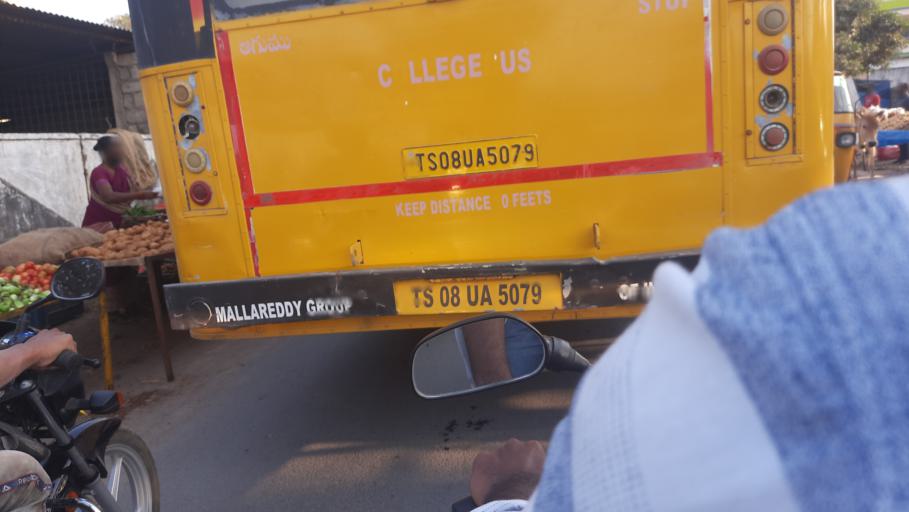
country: IN
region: Telangana
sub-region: Rangareddi
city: Secunderabad
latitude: 17.5096
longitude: 78.5410
